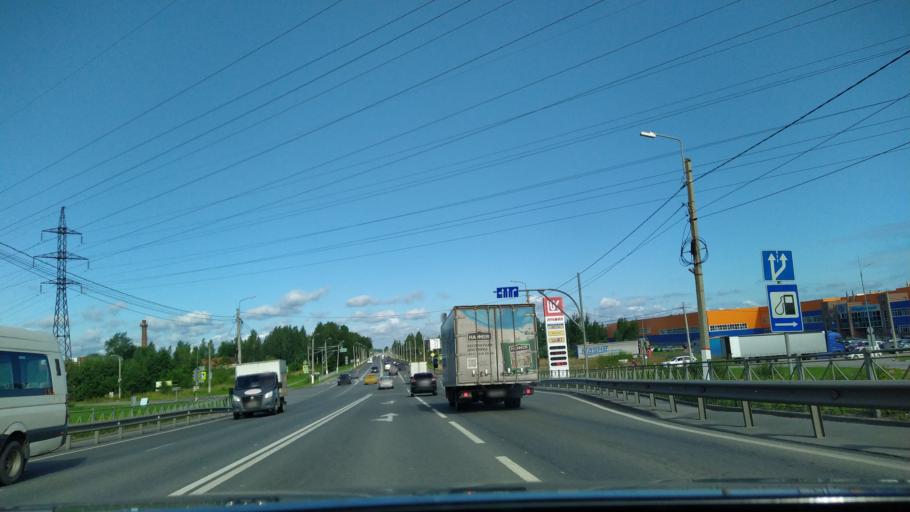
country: RU
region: Leningrad
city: Tosno
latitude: 59.5533
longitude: 30.8545
